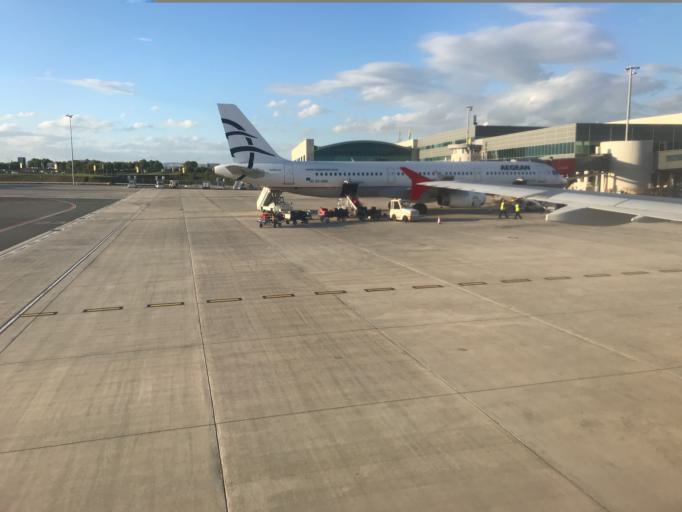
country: CY
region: Larnaka
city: Meneou
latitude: 34.8684
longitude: 33.6091
